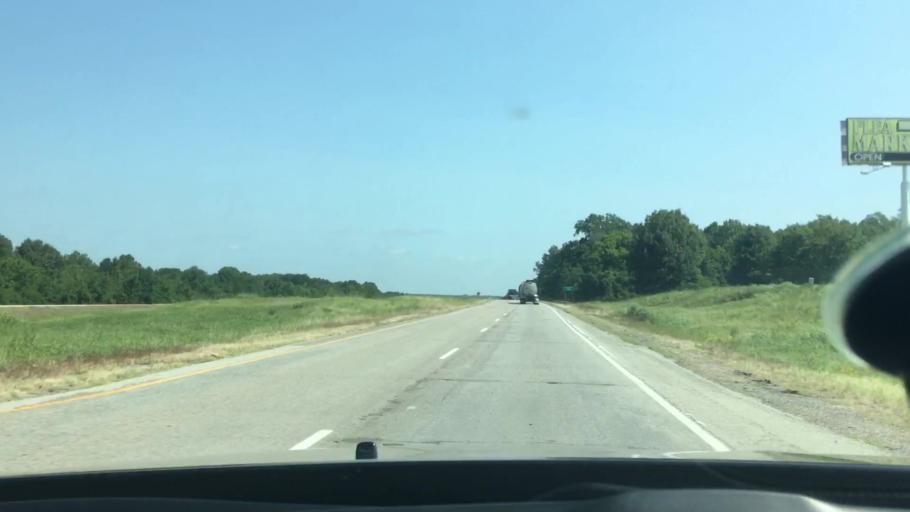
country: US
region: Oklahoma
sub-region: Atoka County
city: Atoka
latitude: 34.2298
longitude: -96.2237
